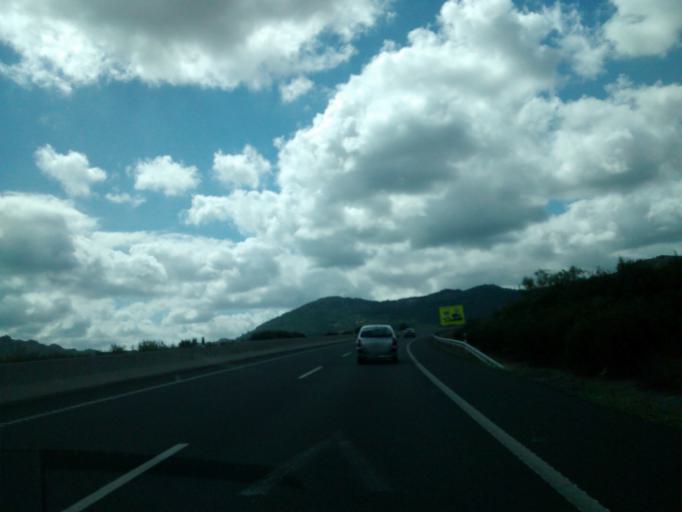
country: ES
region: Extremadura
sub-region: Provincia de Caceres
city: Higuera
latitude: 39.7091
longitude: -5.6921
